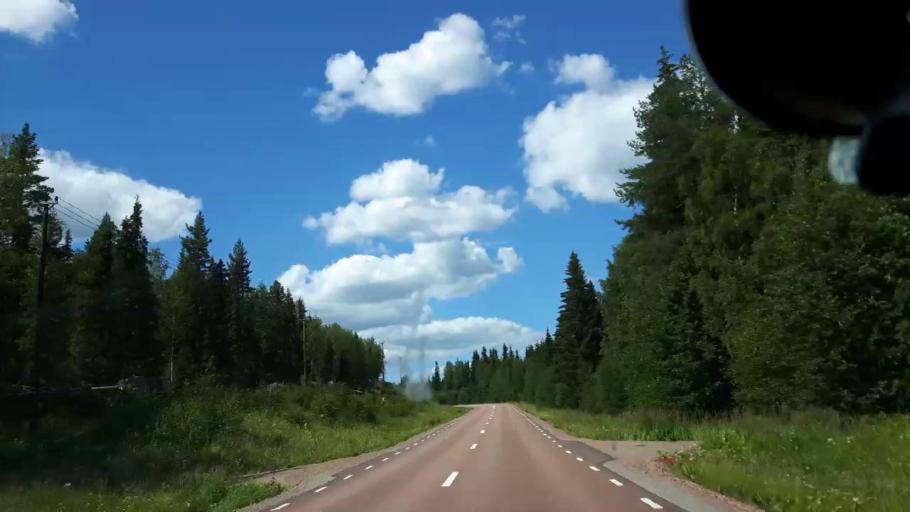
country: SE
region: Jaemtland
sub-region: Ragunda Kommun
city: Hammarstrand
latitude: 63.0169
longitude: 16.6142
